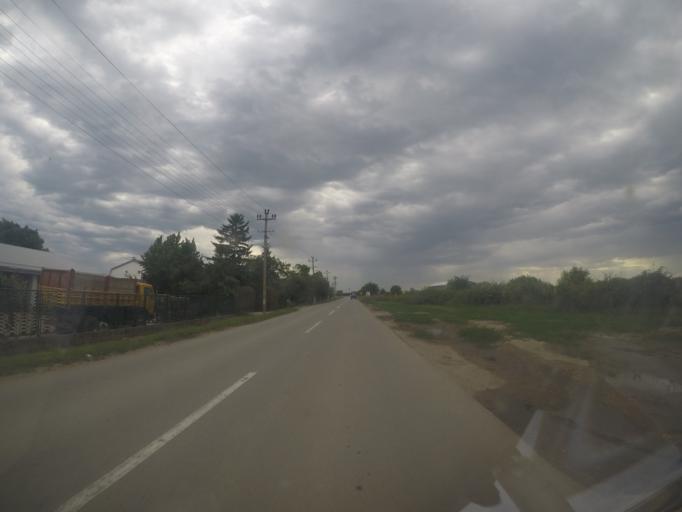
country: RS
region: Autonomna Pokrajina Vojvodina
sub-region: Juznobanatski Okrug
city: Opovo
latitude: 45.0585
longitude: 20.4330
